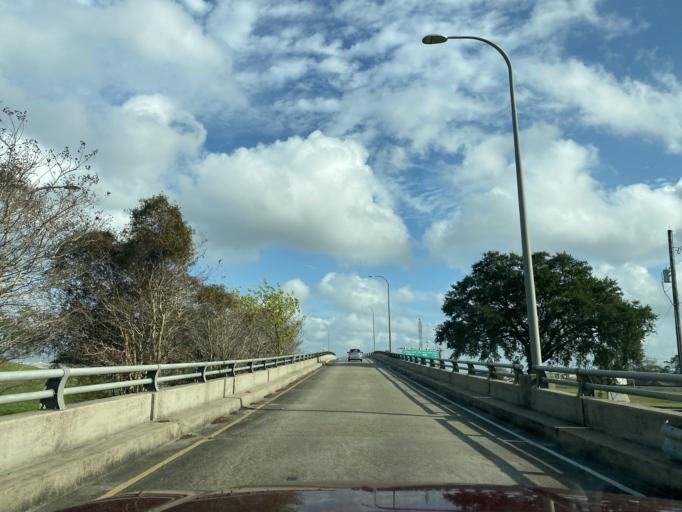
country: US
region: Louisiana
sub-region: Orleans Parish
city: New Orleans
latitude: 30.0311
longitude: -90.0399
